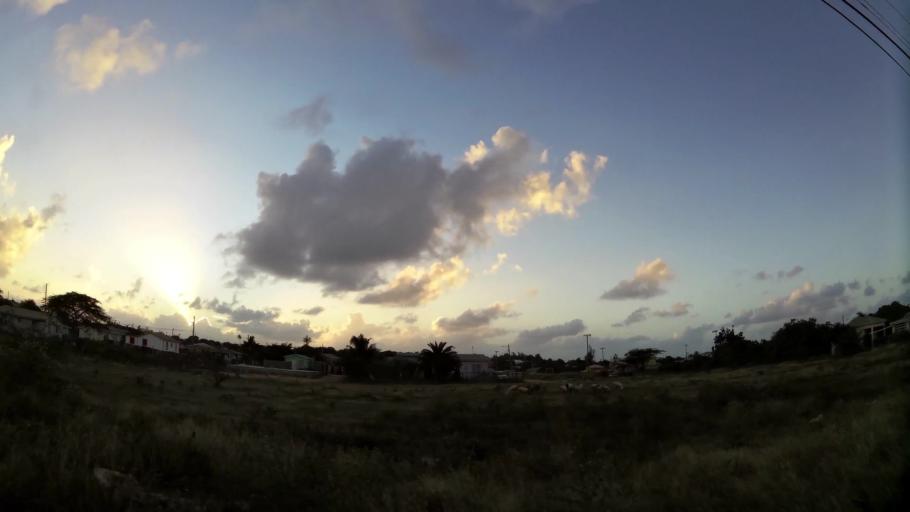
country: AG
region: Saint John
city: Saint John's
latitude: 17.1341
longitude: -61.8393
